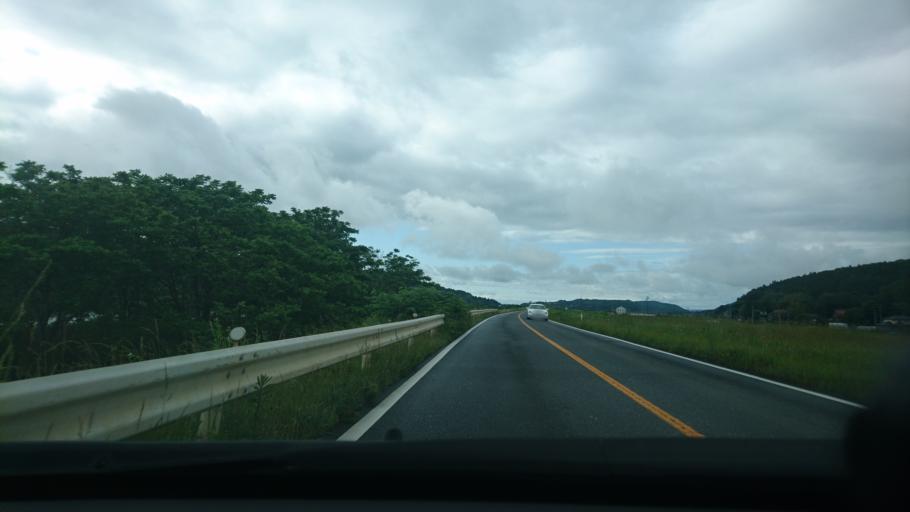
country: JP
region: Miyagi
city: Wakuya
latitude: 38.6315
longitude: 141.2911
